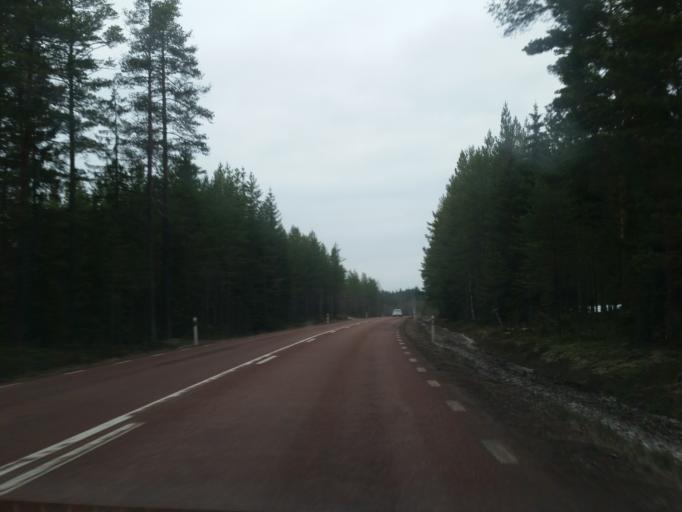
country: SE
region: Dalarna
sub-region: Alvdalens Kommun
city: AElvdalen
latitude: 61.1632
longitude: 14.1159
